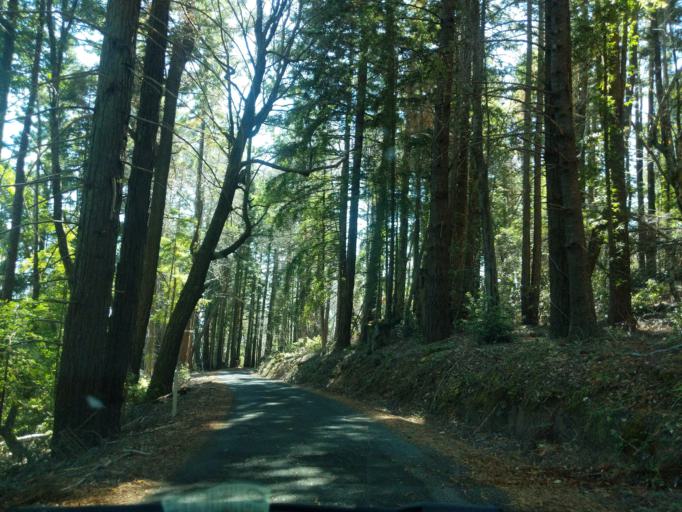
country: US
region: California
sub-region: Sonoma County
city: Monte Rio
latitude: 38.5266
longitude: -123.2275
